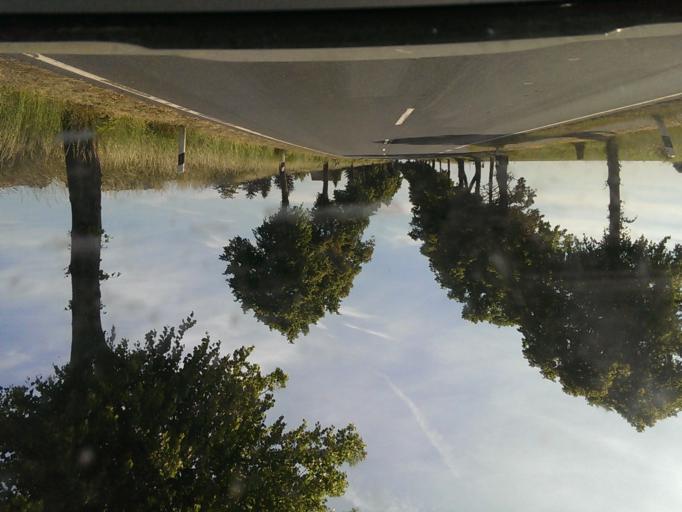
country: DE
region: Lower Saxony
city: Elze
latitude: 52.1345
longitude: 9.7487
